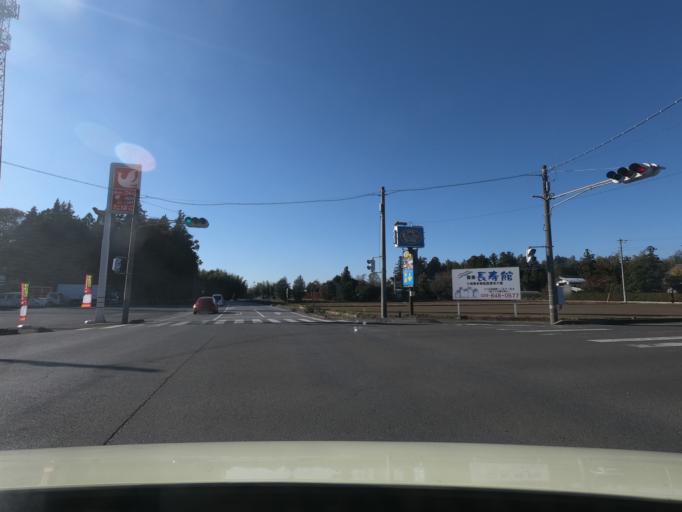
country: JP
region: Ibaraki
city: Ishige
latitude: 36.1200
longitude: 140.0471
